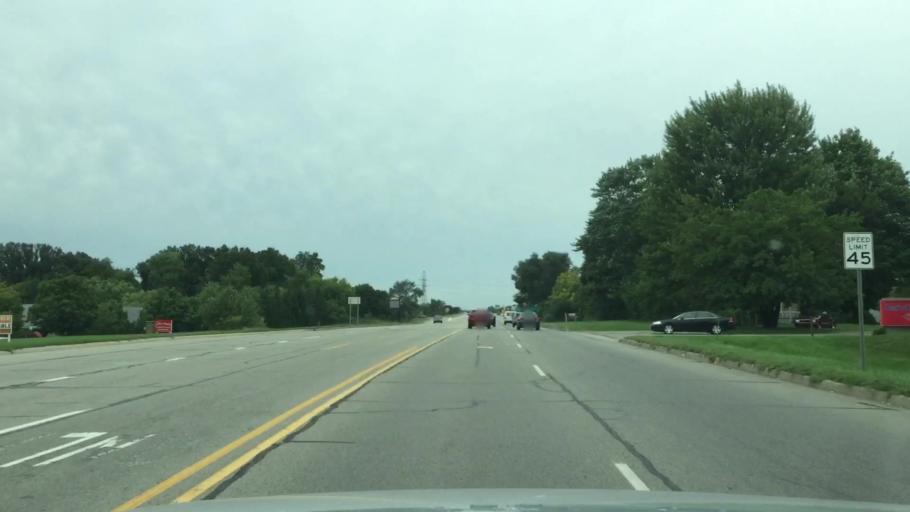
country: US
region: Michigan
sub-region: Washtenaw County
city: Ypsilanti
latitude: 42.2280
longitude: -83.6440
